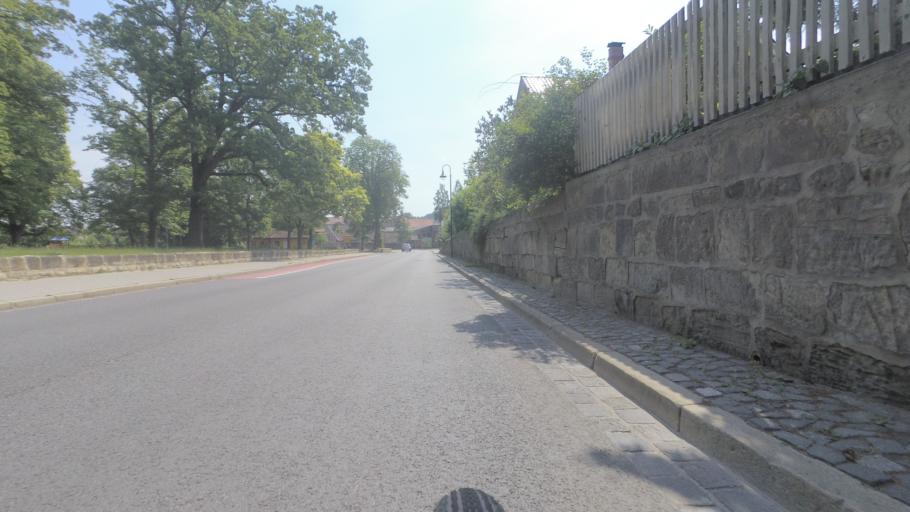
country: DE
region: Saxony-Anhalt
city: Blankenburg
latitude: 51.7913
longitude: 10.9502
